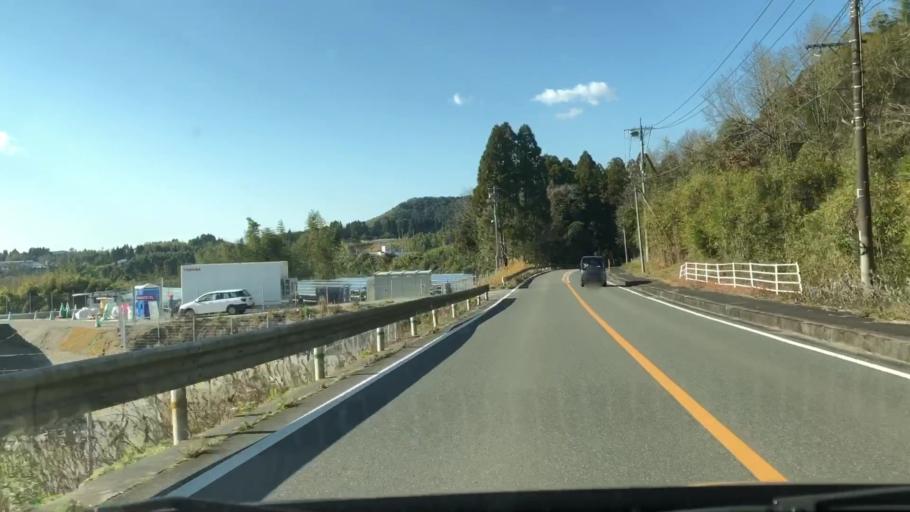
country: JP
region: Kagoshima
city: Satsumasendai
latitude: 31.8567
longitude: 130.3734
